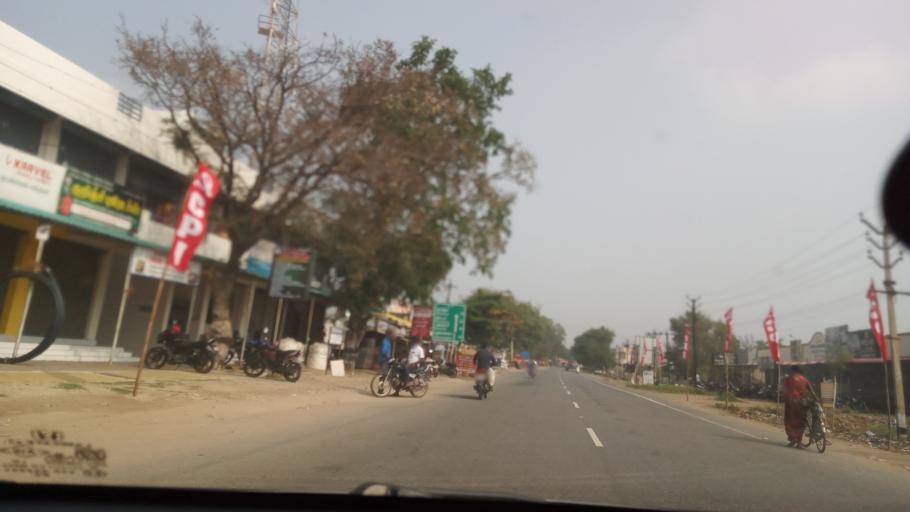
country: IN
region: Tamil Nadu
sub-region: Erode
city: Punjai Puliyampatti
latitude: 11.3584
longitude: 77.1698
